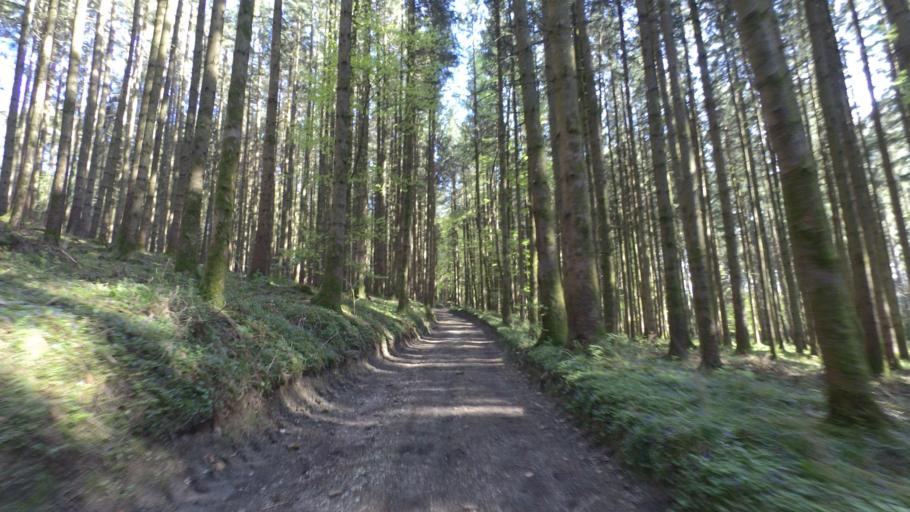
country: DE
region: Bavaria
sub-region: Upper Bavaria
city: Chieming
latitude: 47.8710
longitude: 12.5661
